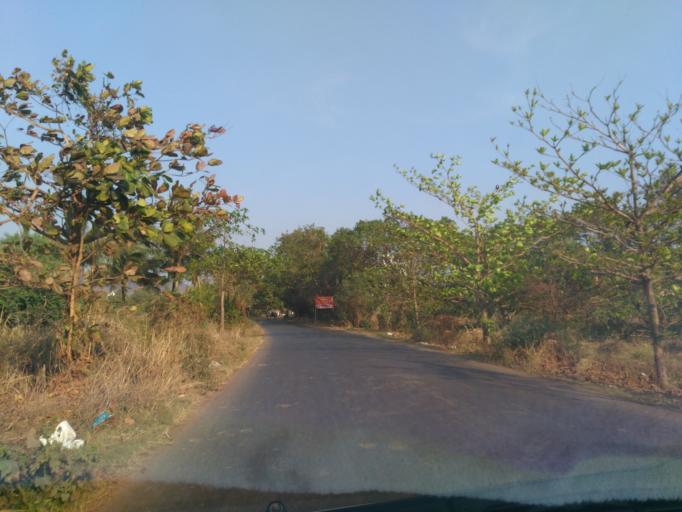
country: IN
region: Maharashtra
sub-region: Raigarh
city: Mhasla
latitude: 18.1671
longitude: 72.9982
